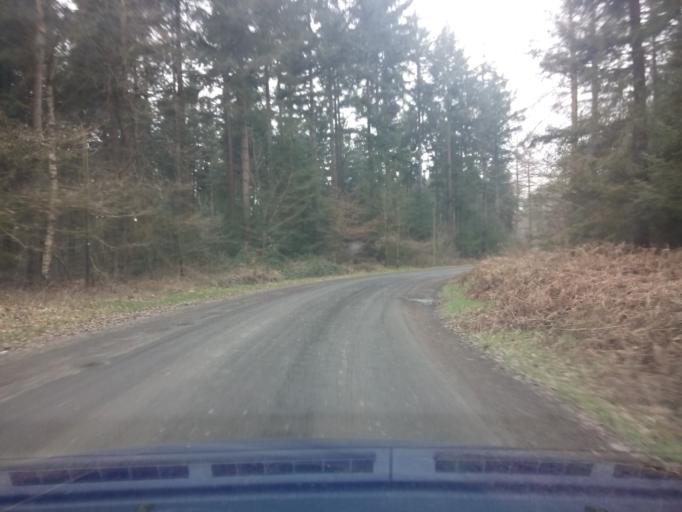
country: DE
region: Lower Saxony
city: Drangstedt
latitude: 53.6136
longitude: 8.7271
